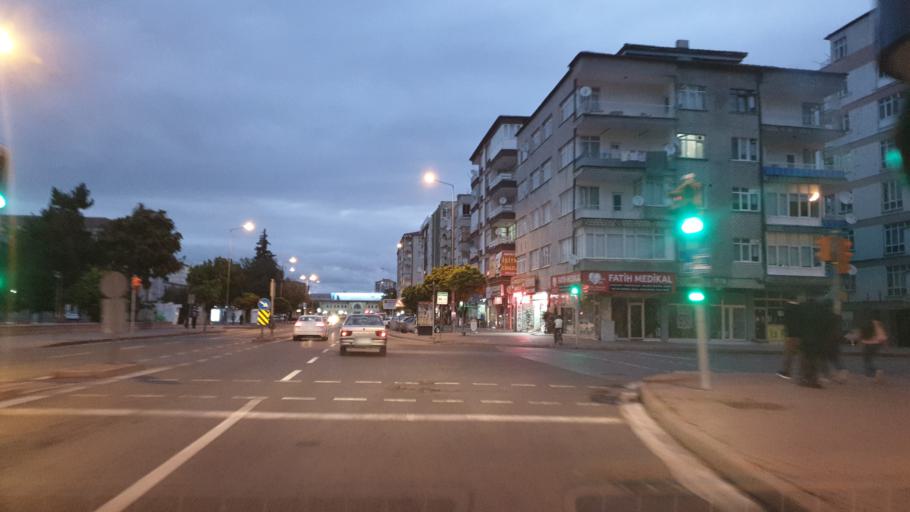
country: TR
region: Kayseri
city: Kayseri
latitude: 38.7269
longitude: 35.4798
